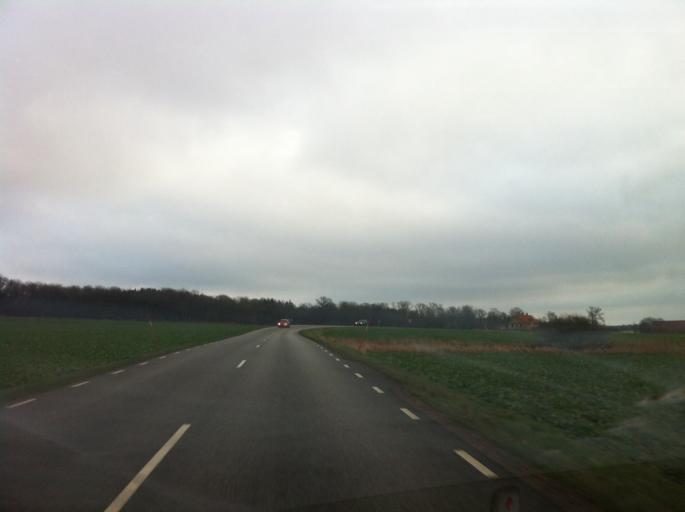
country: SE
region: Skane
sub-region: Hoors Kommun
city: Loberod
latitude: 55.7014
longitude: 13.5782
